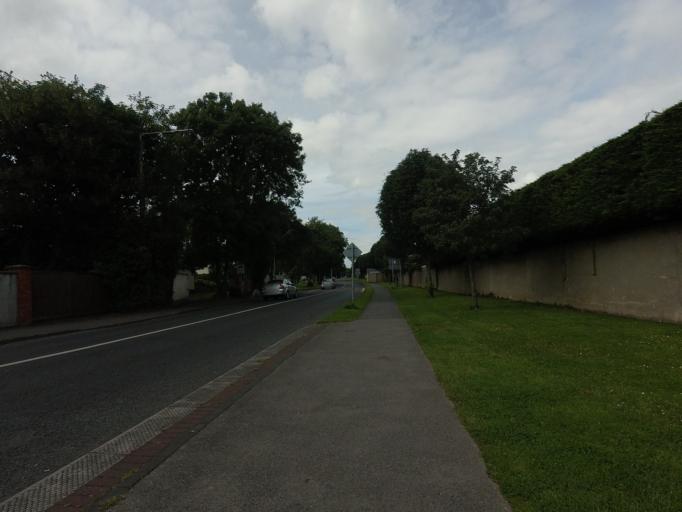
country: IE
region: Leinster
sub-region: Fingal County
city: Blanchardstown
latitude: 53.3779
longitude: -6.3922
